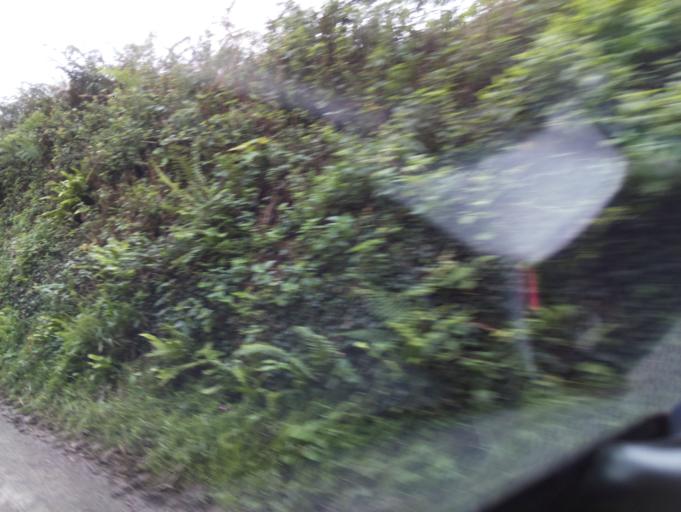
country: GB
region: England
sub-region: Devon
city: Kingsbridge
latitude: 50.2956
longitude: -3.7169
